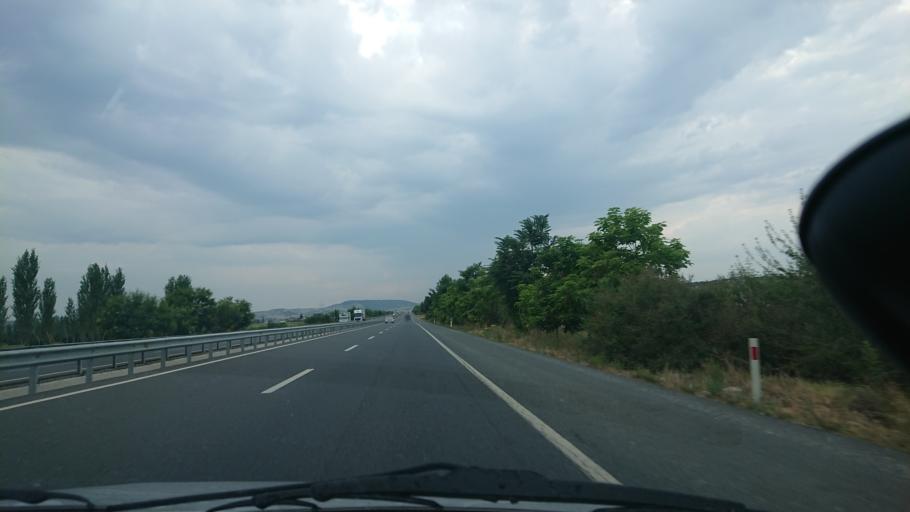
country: TR
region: Manisa
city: Selendi
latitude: 38.6208
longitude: 28.9143
